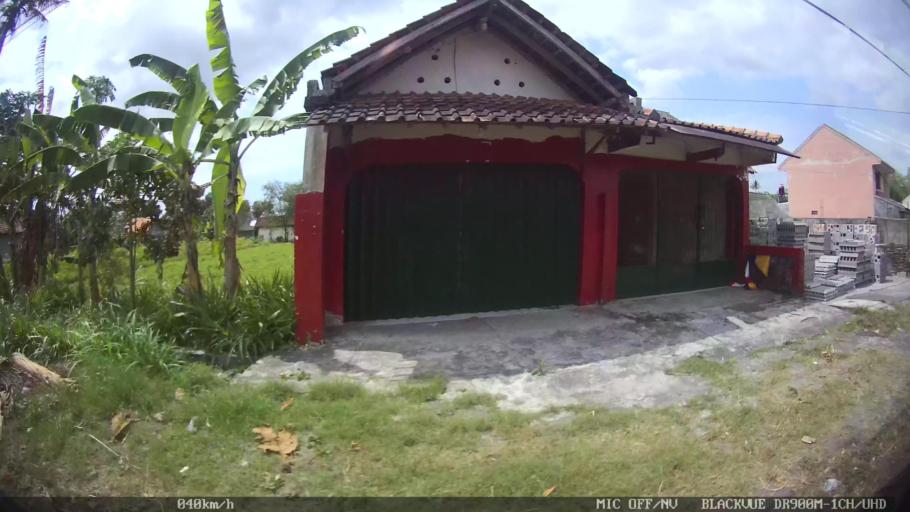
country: ID
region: Daerah Istimewa Yogyakarta
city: Depok
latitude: -7.8012
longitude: 110.4544
